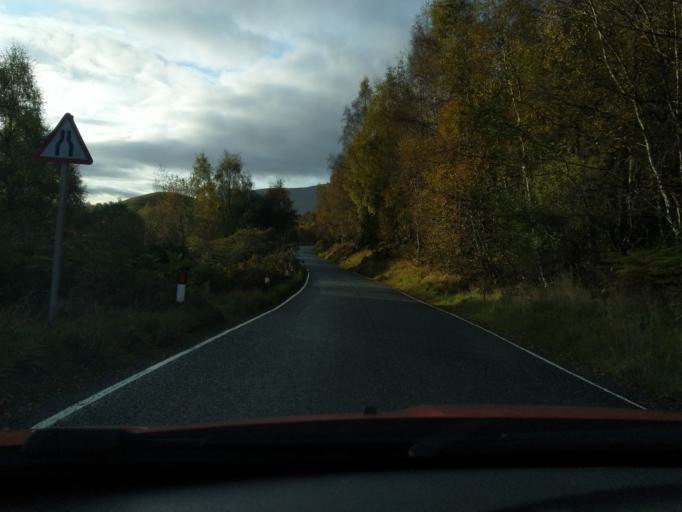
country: GB
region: Scotland
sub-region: Perth and Kinross
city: Aberfeldy
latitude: 56.7256
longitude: -4.1146
